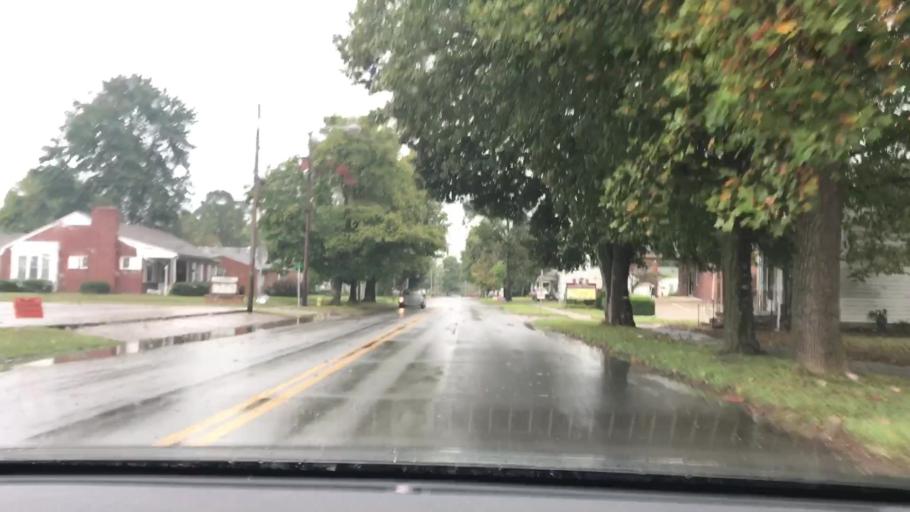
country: US
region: Kentucky
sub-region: McLean County
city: Calhoun
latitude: 37.5390
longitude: -87.2584
